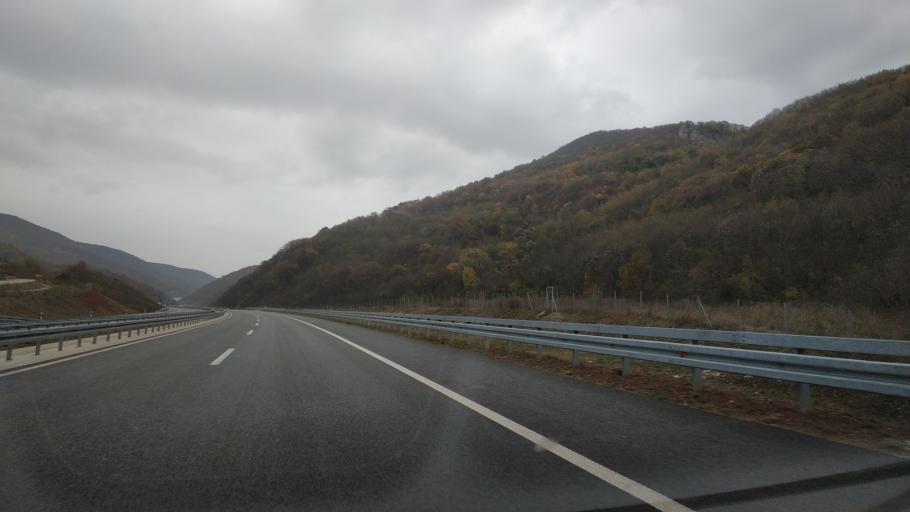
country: RS
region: Central Serbia
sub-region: Nisavski Okrug
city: Niska Banja
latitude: 43.2993
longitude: 22.0645
